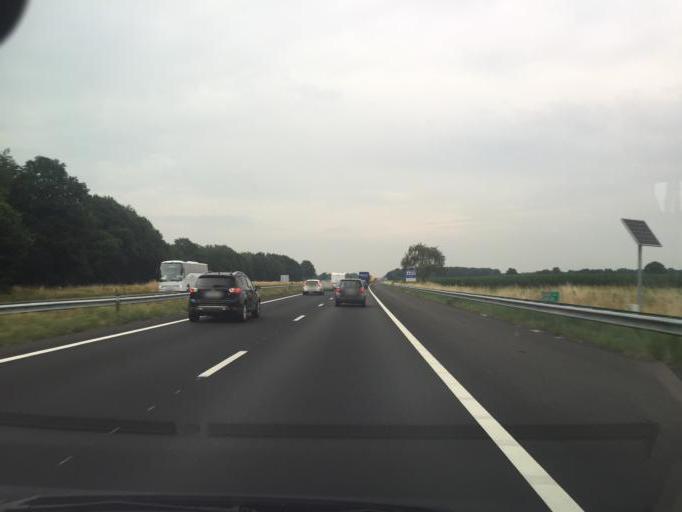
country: NL
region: North Brabant
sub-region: Gemeente Asten
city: Asten
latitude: 51.4128
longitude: 5.7863
